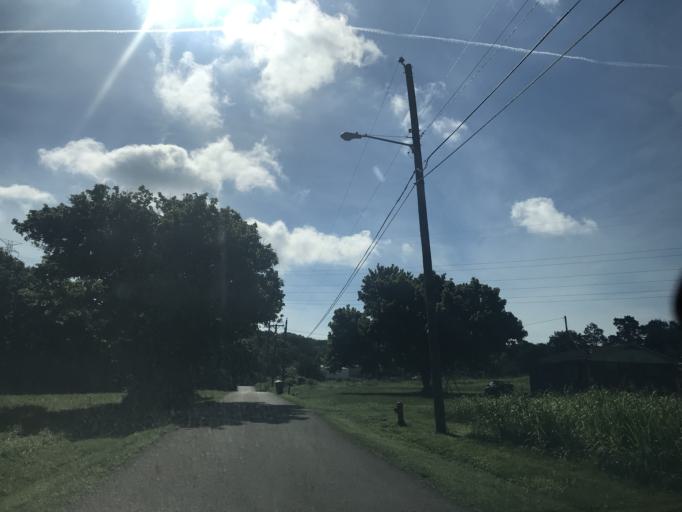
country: US
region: Tennessee
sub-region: Davidson County
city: Nashville
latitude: 36.2034
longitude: -86.8425
